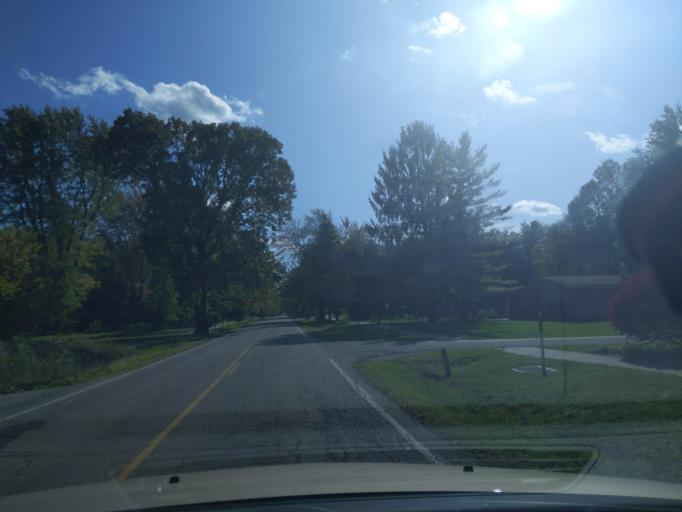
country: US
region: Michigan
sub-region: Ingham County
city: Haslett
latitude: 42.7459
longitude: -84.3931
